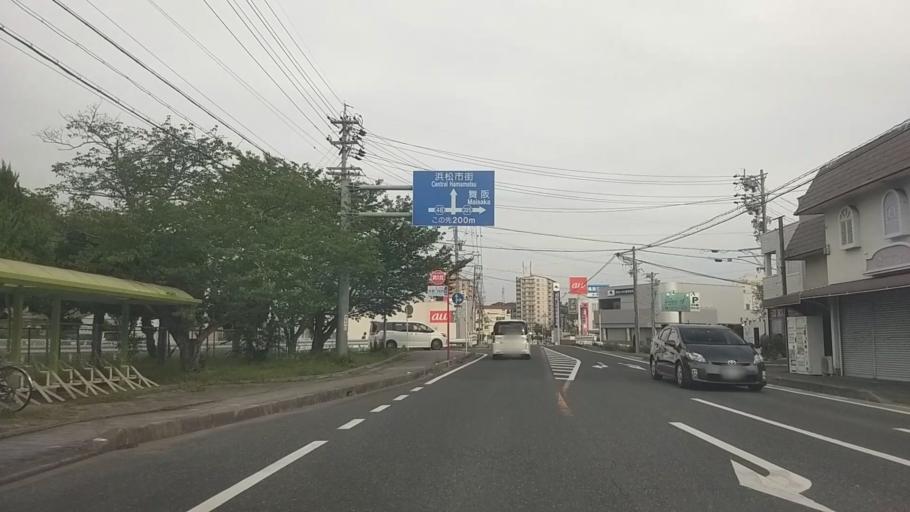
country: JP
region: Shizuoka
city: Hamamatsu
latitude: 34.7247
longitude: 137.6963
